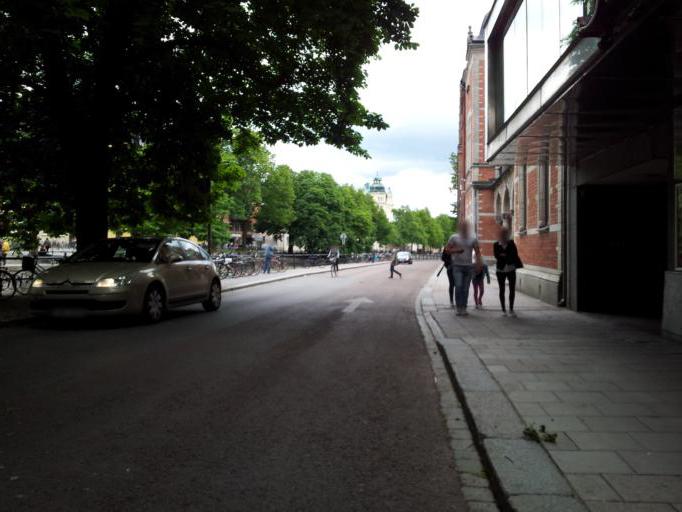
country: SE
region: Uppsala
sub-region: Uppsala Kommun
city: Uppsala
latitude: 59.8576
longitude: 17.6375
